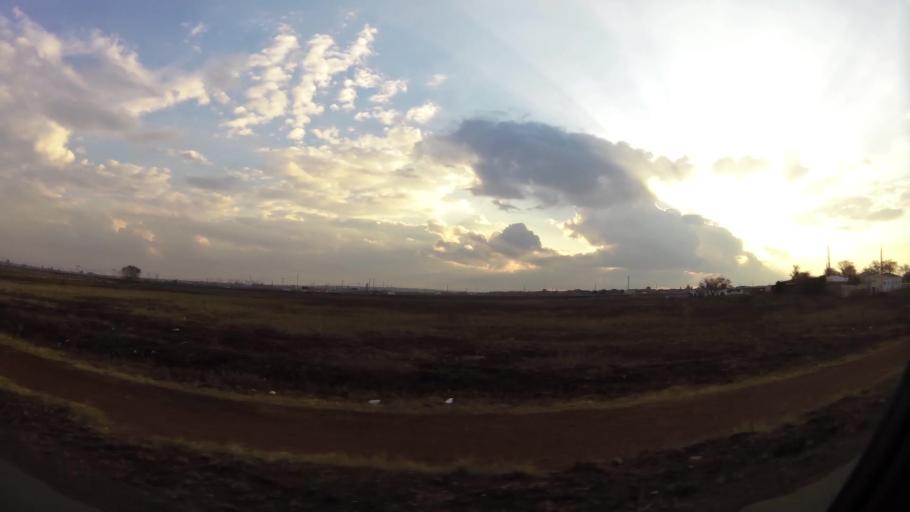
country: ZA
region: Gauteng
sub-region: City of Johannesburg Metropolitan Municipality
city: Orange Farm
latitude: -26.5428
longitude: 27.8329
